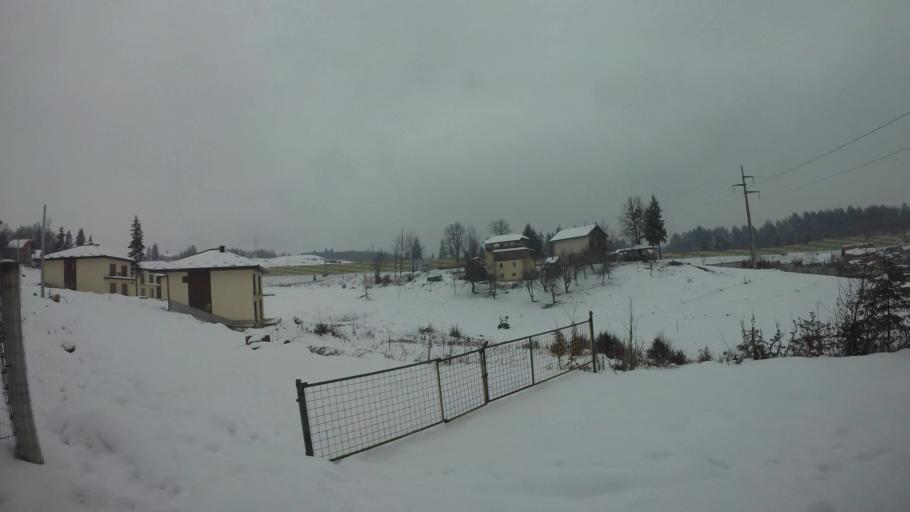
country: BA
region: Federation of Bosnia and Herzegovina
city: Hadzici
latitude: 43.8605
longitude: 18.2666
